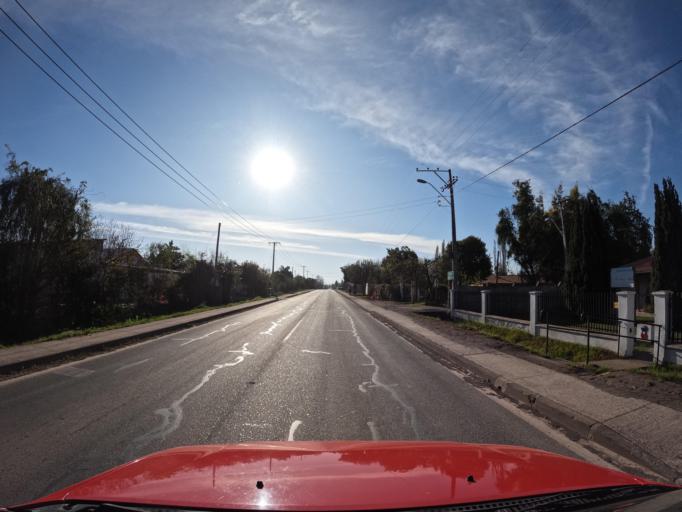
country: CL
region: Maule
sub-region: Provincia de Curico
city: Teno
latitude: -34.9564
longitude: -70.9767
